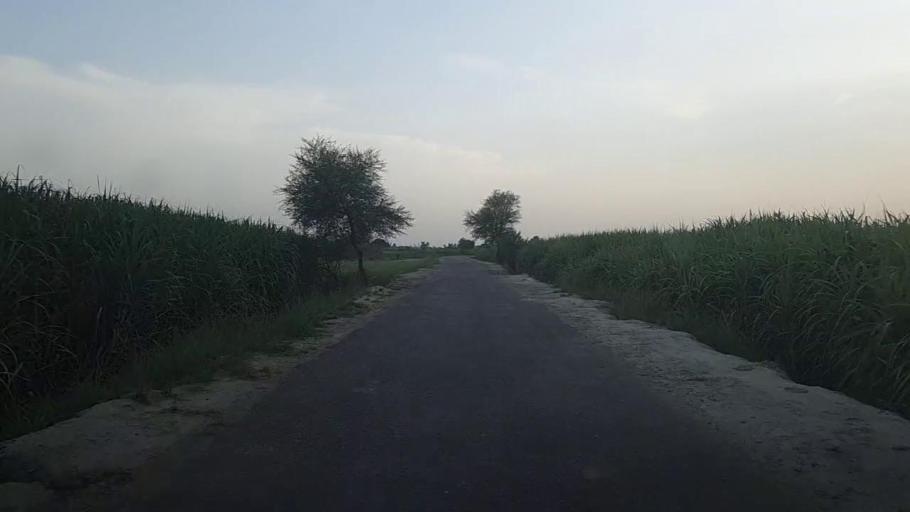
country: PK
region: Sindh
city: Ubauro
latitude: 28.3563
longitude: 69.7838
